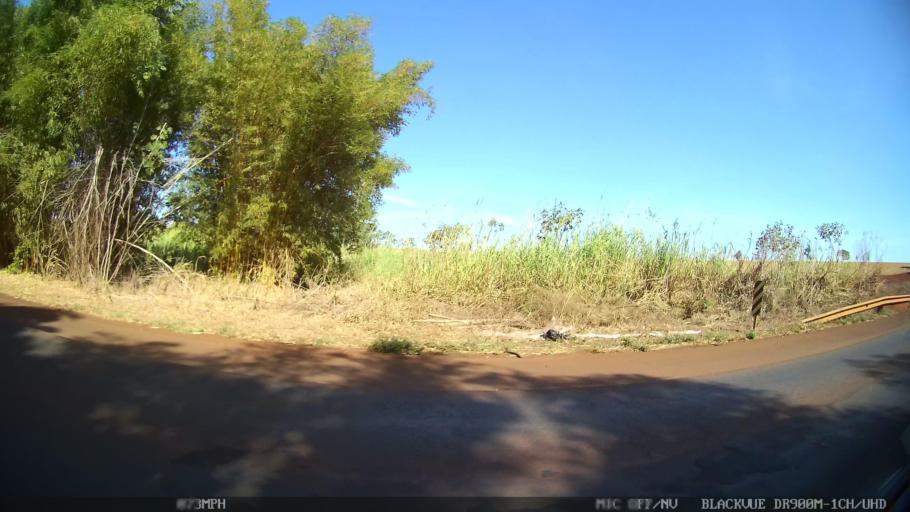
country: BR
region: Sao Paulo
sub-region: Sao Joaquim Da Barra
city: Sao Joaquim da Barra
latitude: -20.5094
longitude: -47.9138
